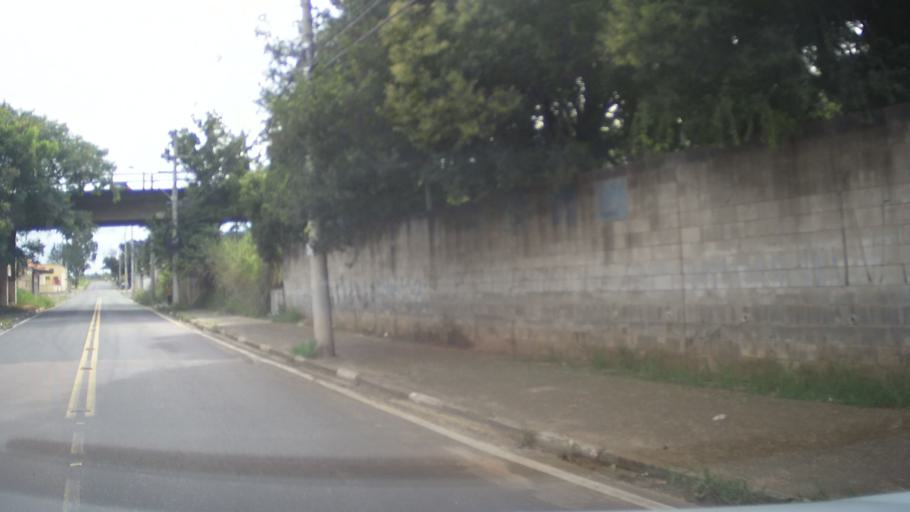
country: BR
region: Sao Paulo
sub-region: Hortolandia
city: Hortolandia
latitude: -22.8839
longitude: -47.1439
